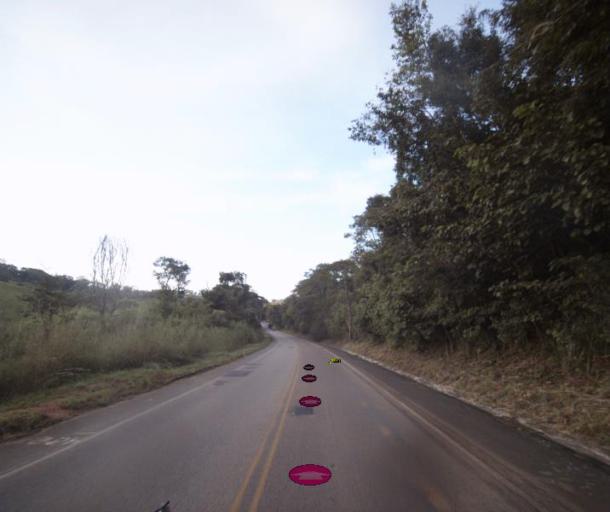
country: BR
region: Goias
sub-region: Abadiania
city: Abadiania
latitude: -16.1252
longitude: -48.8946
